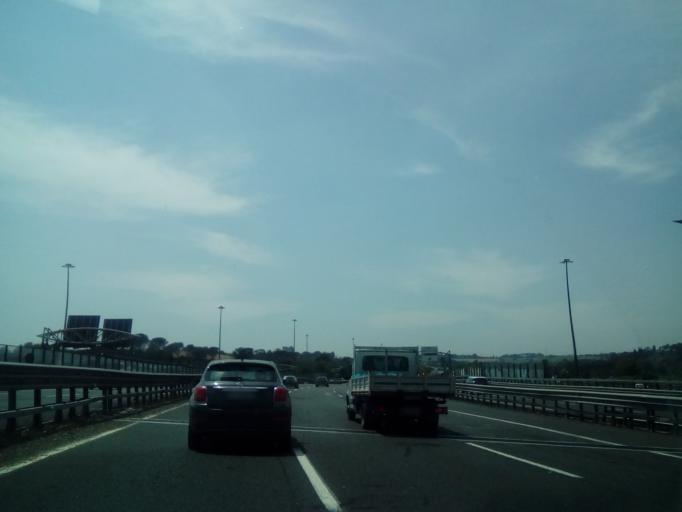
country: IT
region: Latium
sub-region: Citta metropolitana di Roma Capitale
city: Monte Caminetto
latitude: 41.9861
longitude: 12.4941
